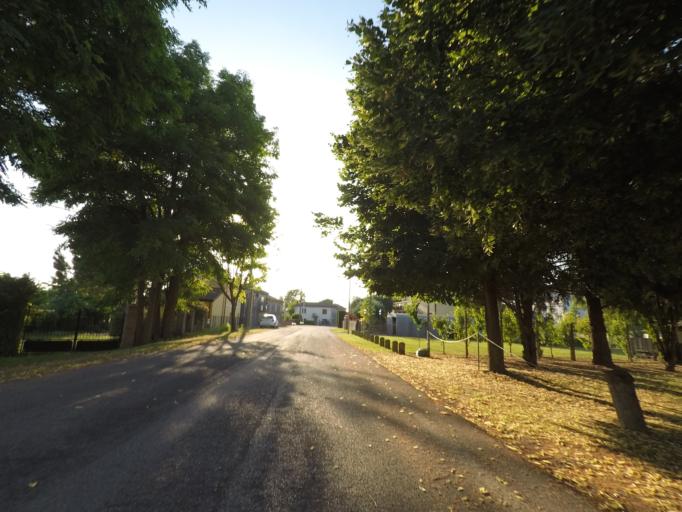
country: IT
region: Veneto
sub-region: Provincia di Rovigo
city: Villamarzana
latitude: 45.0220
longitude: 11.6782
